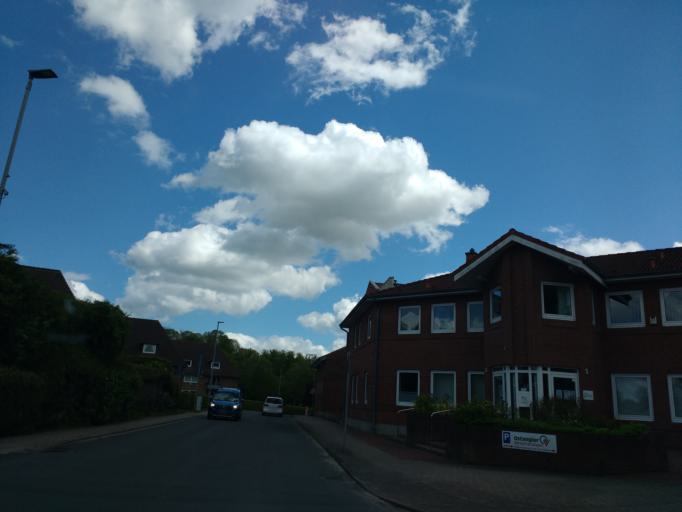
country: DE
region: Schleswig-Holstein
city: Kappeln
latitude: 54.6634
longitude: 9.9238
